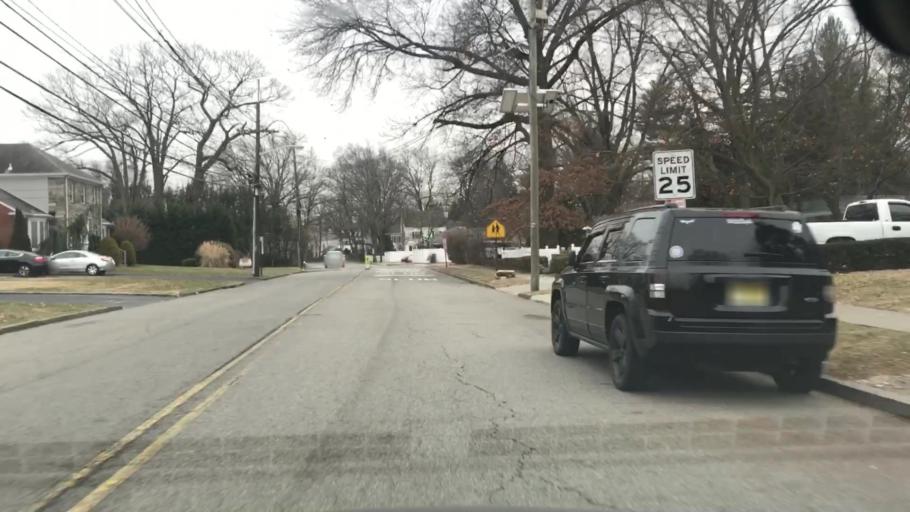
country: US
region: New Jersey
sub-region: Union County
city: Hillside
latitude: 40.6853
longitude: -74.2188
